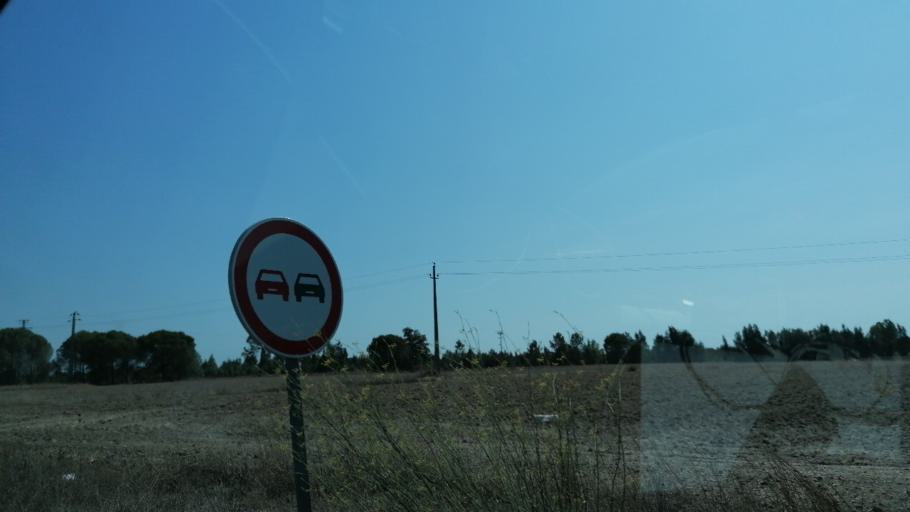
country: PT
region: Santarem
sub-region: Benavente
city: Poceirao
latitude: 38.7250
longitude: -8.6423
